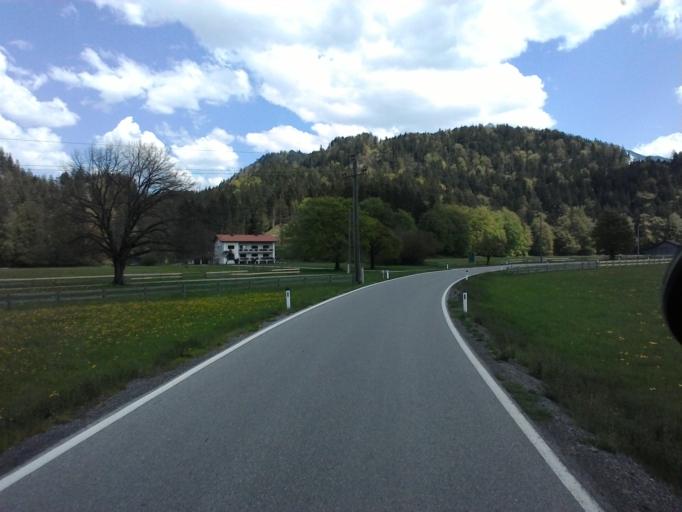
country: AT
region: Tyrol
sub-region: Politischer Bezirk Reutte
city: Musau
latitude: 47.5412
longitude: 10.6849
